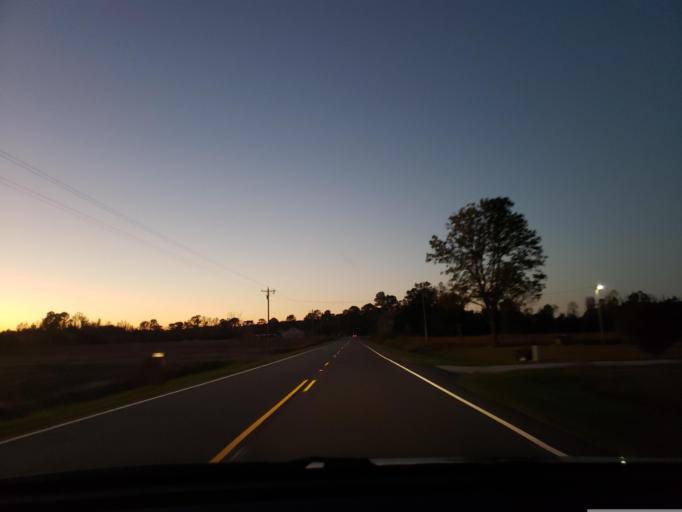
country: US
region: North Carolina
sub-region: Duplin County
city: Kenansville
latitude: 34.9223
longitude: -77.9346
